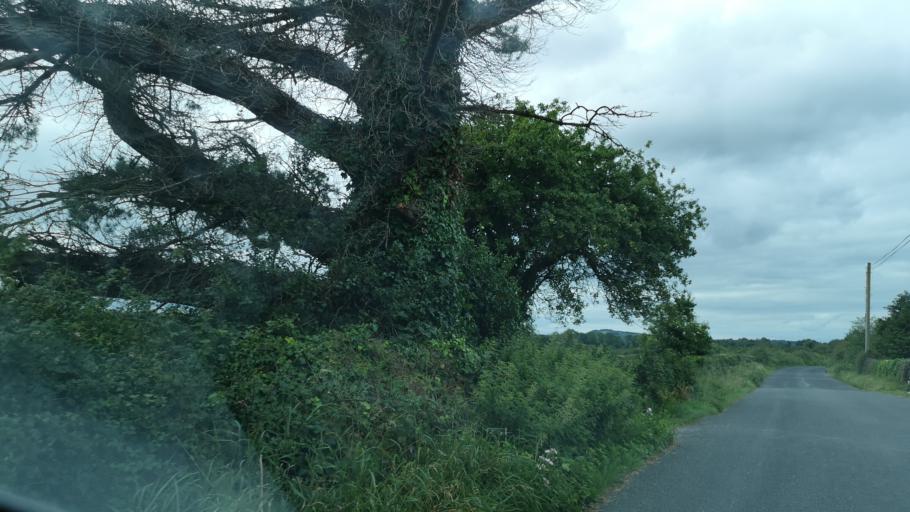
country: IE
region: Connaught
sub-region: County Galway
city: Loughrea
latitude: 53.1561
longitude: -8.4476
